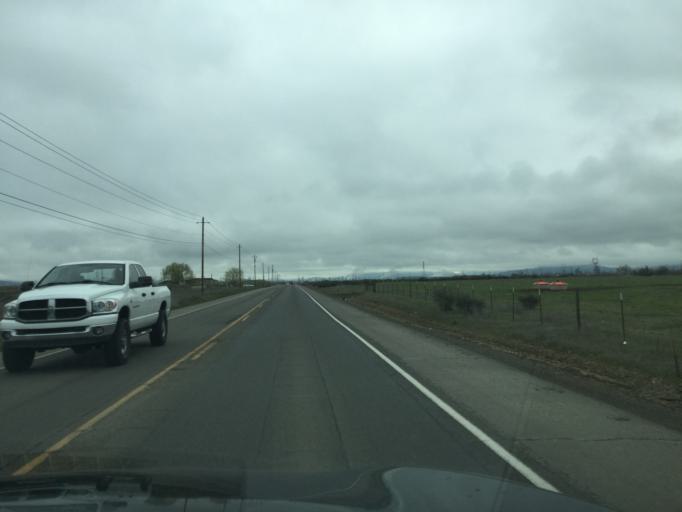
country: US
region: Oregon
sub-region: Jackson County
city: Central Point
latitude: 42.4287
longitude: -122.9324
